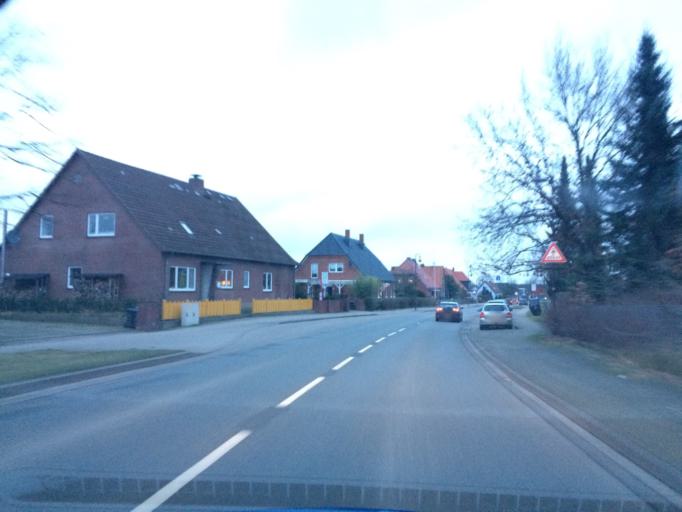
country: DE
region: Lower Saxony
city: Bardowick
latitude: 53.2908
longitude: 10.3799
